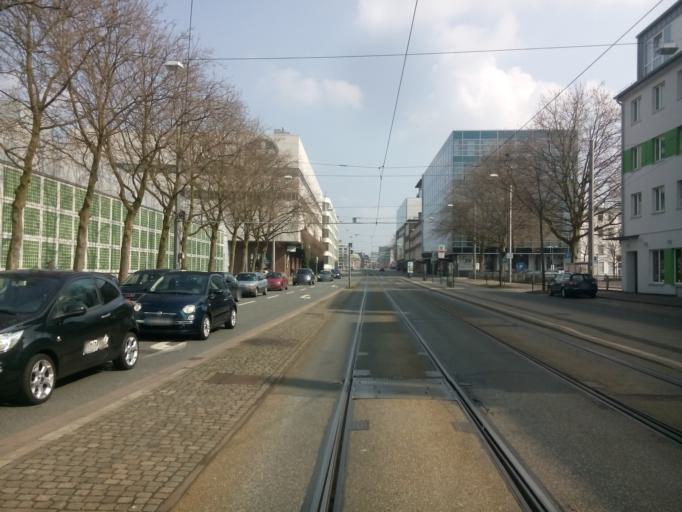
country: DE
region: Bremen
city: Bremen
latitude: 53.0751
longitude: 8.7942
